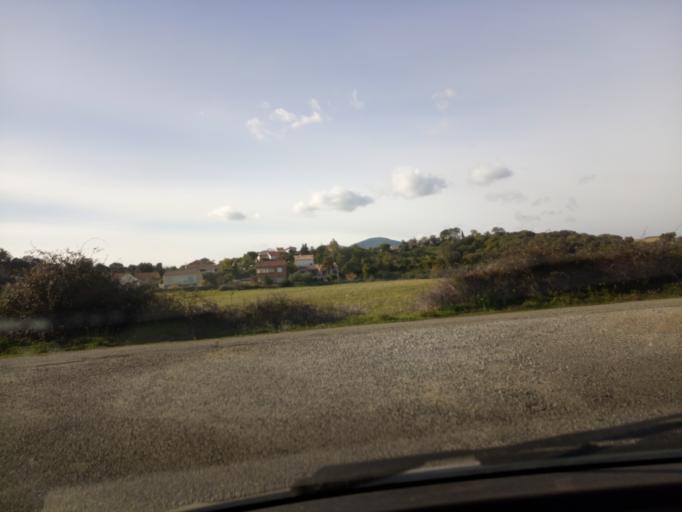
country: FR
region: Corsica
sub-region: Departement de la Haute-Corse
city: Linguizzetta
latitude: 42.2625
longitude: 9.5448
